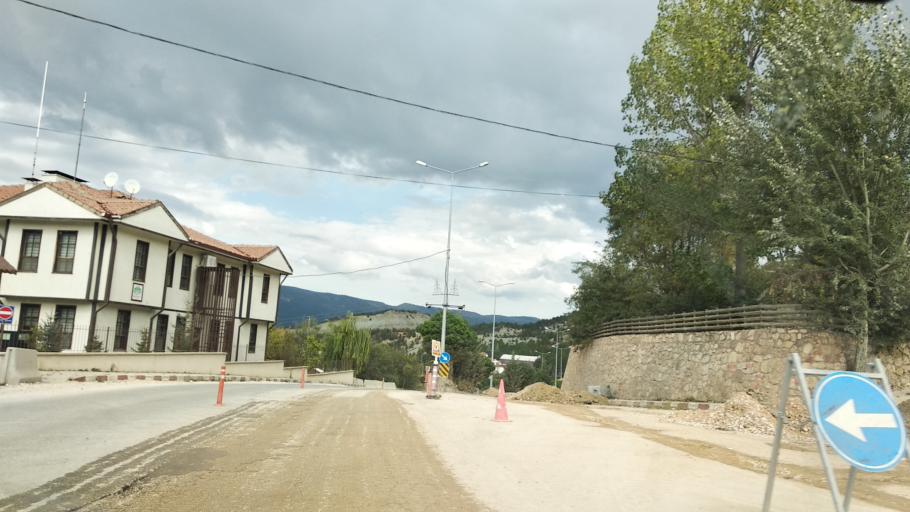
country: TR
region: Bolu
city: Mudurnu
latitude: 40.4744
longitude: 31.2095
